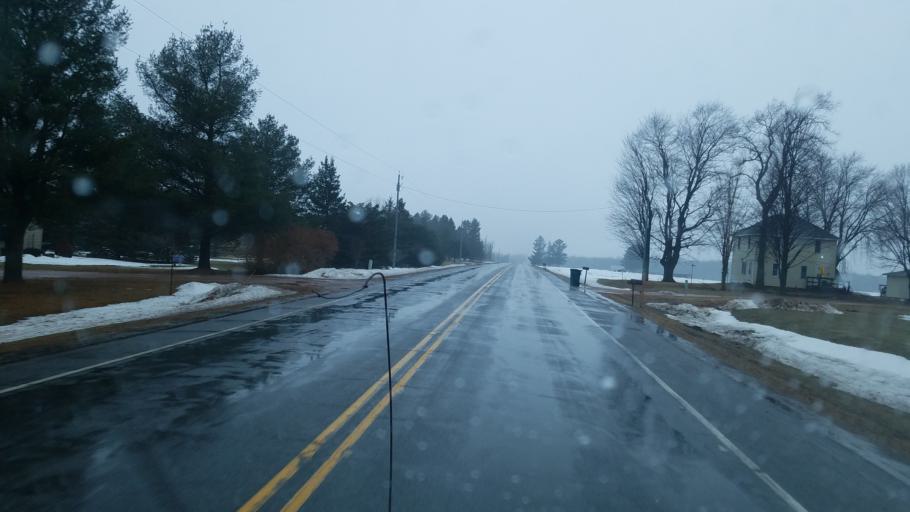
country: US
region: Wisconsin
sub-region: Marathon County
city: Spencer
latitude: 44.6777
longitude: -90.2687
